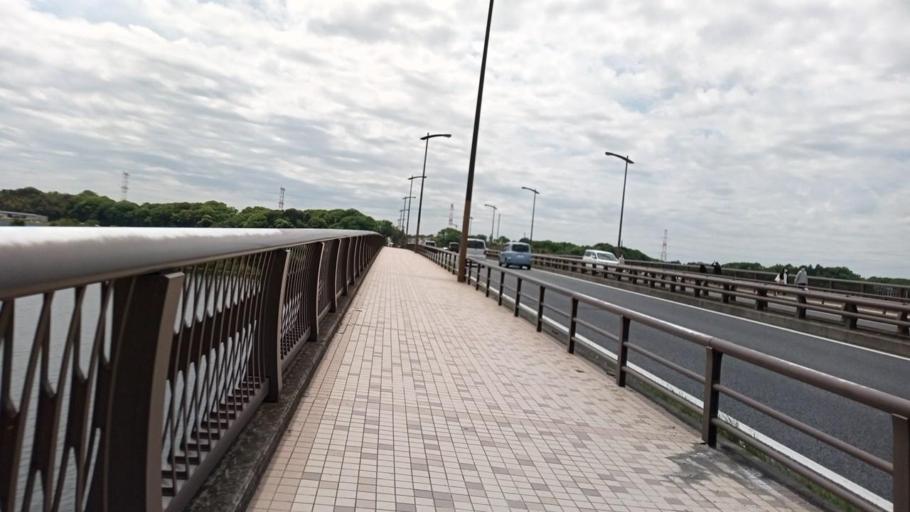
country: JP
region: Chiba
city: Abiko
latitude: 35.8611
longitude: 140.0257
